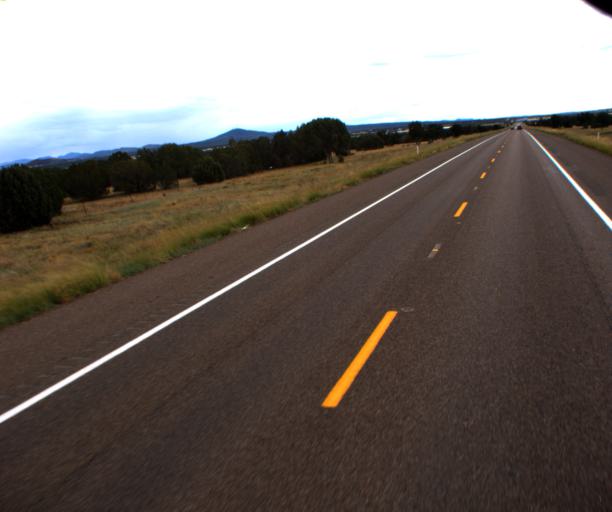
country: US
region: Arizona
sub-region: Navajo County
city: Show Low
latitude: 34.2800
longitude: -110.0270
